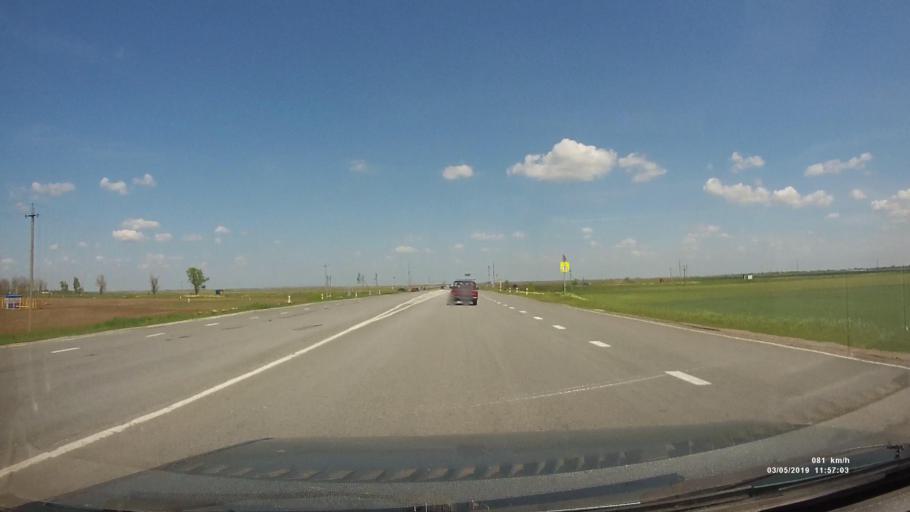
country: RU
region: Rostov
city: Bagayevskaya
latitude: 47.2021
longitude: 40.3065
